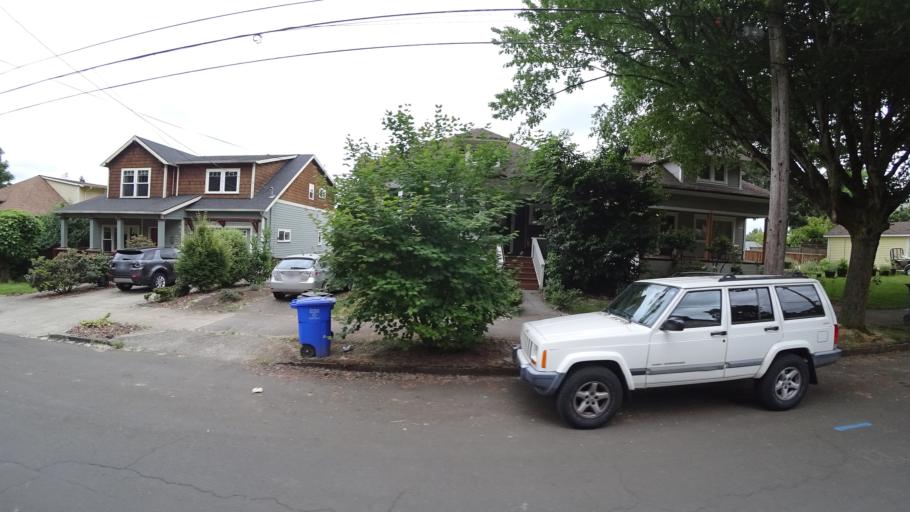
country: US
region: Oregon
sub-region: Multnomah County
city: Portland
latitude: 45.4987
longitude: -122.6569
